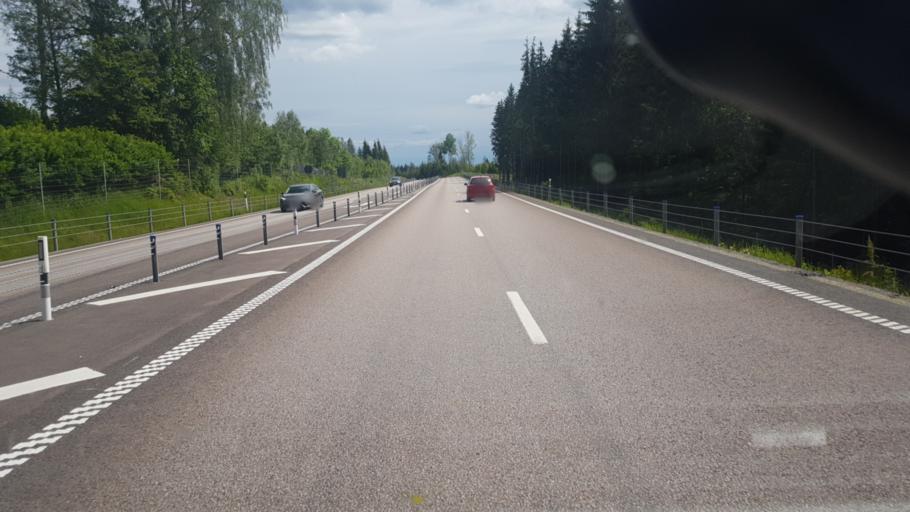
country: SE
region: Vaermland
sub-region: Eda Kommun
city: Amotfors
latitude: 59.7628
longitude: 12.3982
